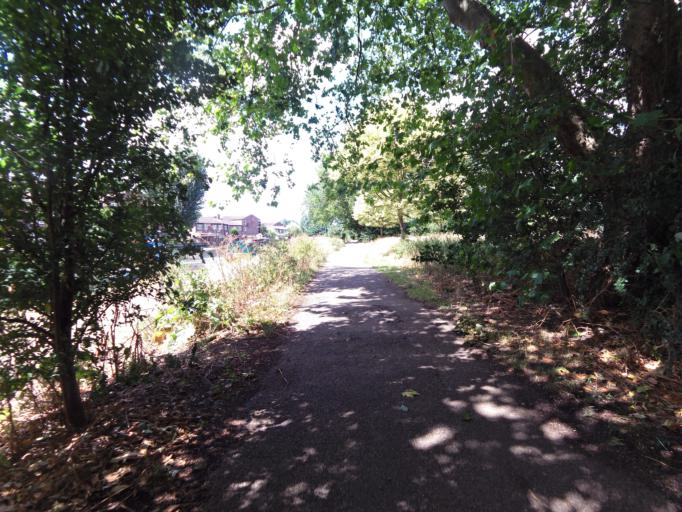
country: GB
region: England
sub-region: Greater London
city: Hackney
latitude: 51.5523
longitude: -0.0308
